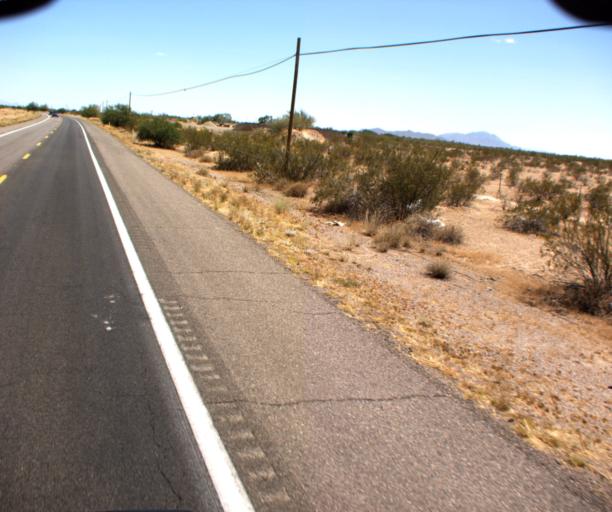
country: US
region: Arizona
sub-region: Pinal County
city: Florence
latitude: 32.9905
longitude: -111.3634
